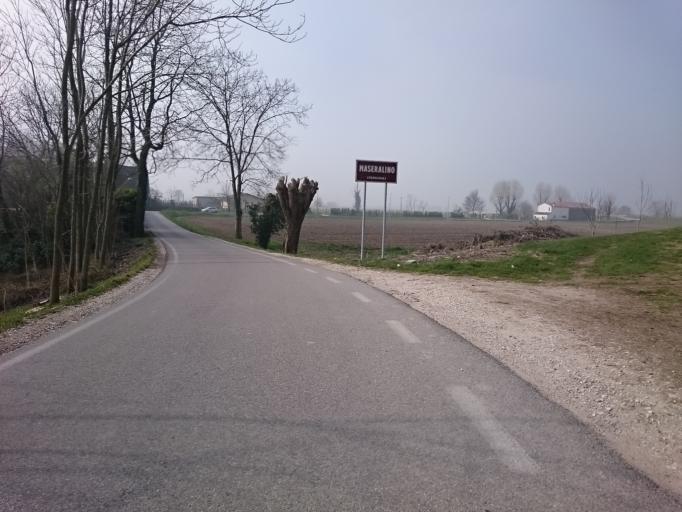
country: IT
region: Veneto
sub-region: Provincia di Padova
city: Due Carrare
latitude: 45.2729
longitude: 11.8284
